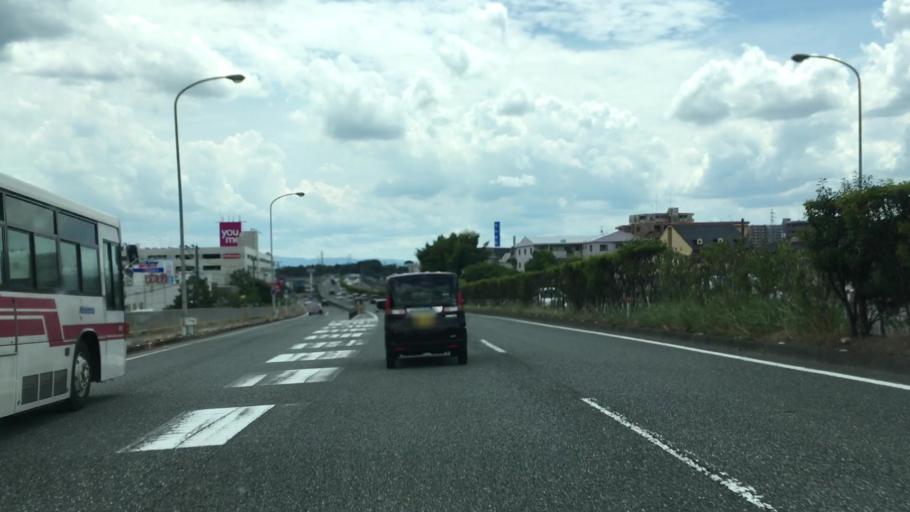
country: JP
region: Fukuoka
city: Chikushino-shi
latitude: 33.4871
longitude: 130.5361
